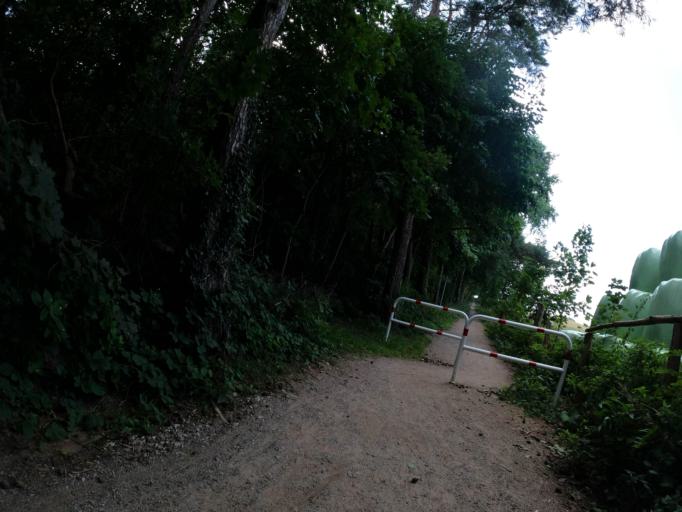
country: DE
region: Mecklenburg-Vorpommern
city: Malchow
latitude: 53.4947
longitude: 12.4369
